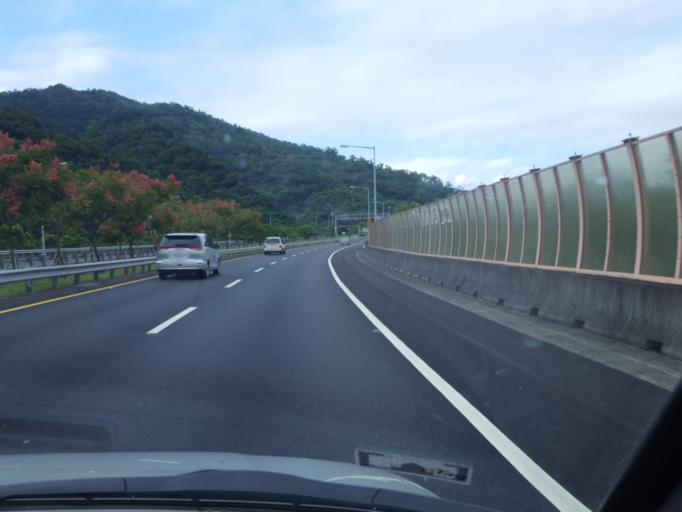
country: TW
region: Taiwan
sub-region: Yilan
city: Yilan
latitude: 24.8431
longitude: 121.7894
